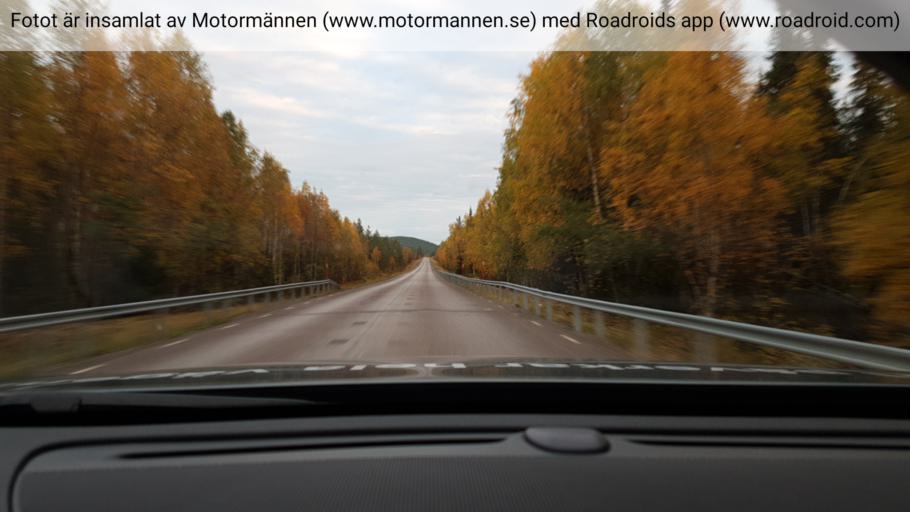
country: SE
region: Norrbotten
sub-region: Jokkmokks Kommun
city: Jokkmokk
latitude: 66.0246
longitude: 20.1324
